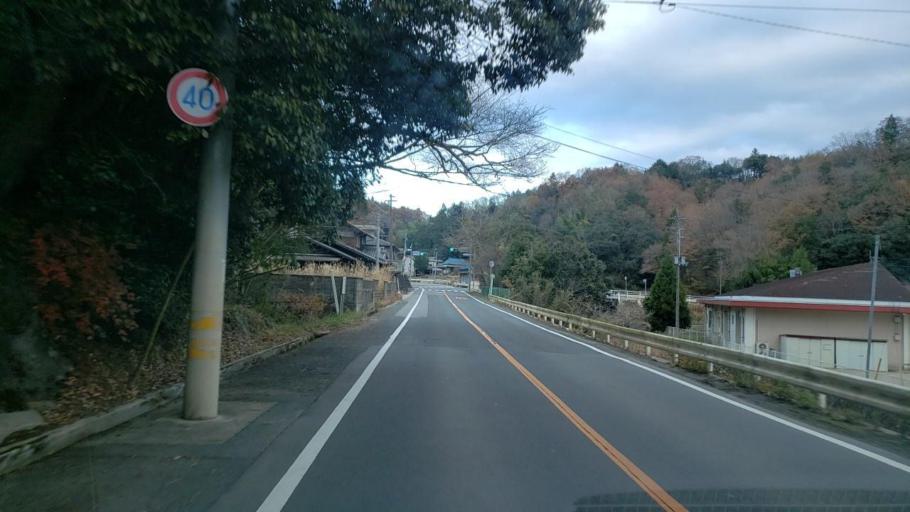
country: JP
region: Tokushima
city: Wakimachi
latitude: 34.1863
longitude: 134.1701
